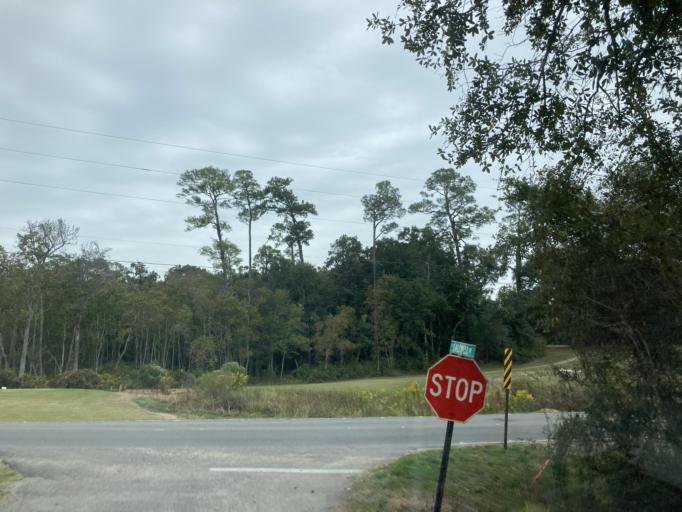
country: US
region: Mississippi
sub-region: Jackson County
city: Gulf Hills
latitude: 30.4254
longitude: -88.8341
